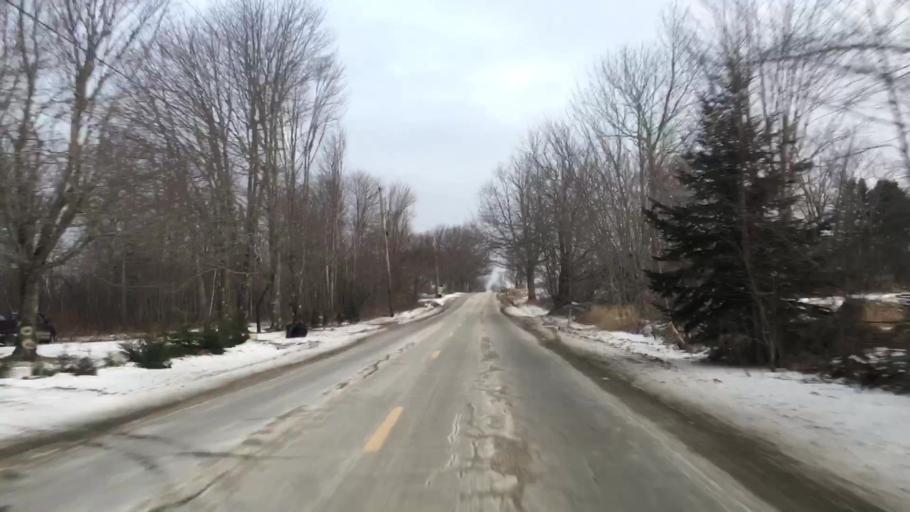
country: US
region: Maine
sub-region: Hancock County
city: Franklin
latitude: 44.7059
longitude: -68.3405
